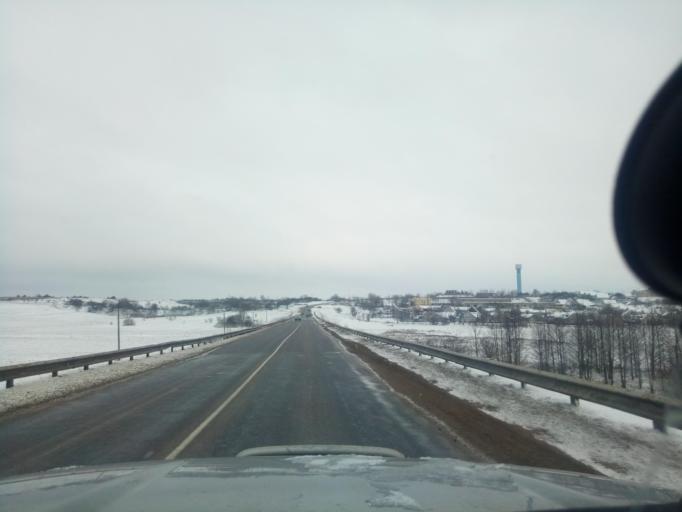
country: BY
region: Minsk
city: Kapyl'
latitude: 53.1429
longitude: 27.0807
